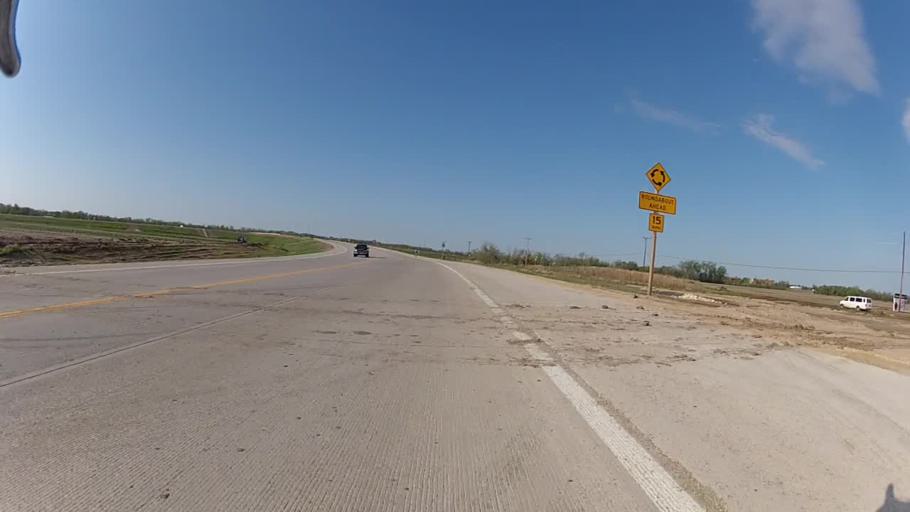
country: US
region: Kansas
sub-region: Riley County
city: Manhattan
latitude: 39.1593
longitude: -96.6442
